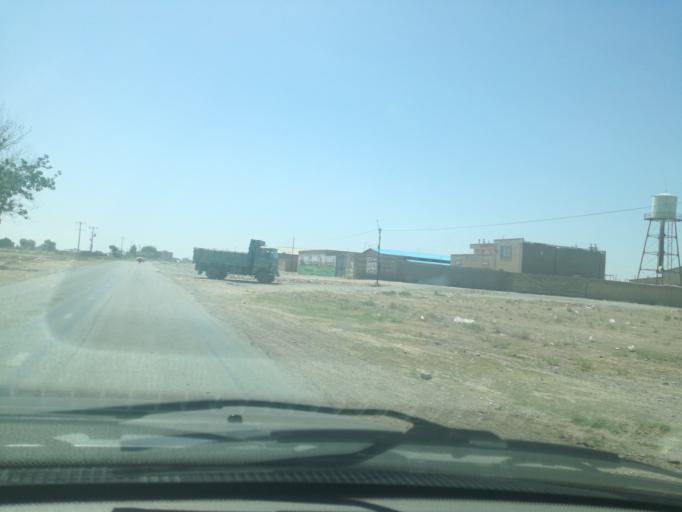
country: IR
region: Razavi Khorasan
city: Sarakhs
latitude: 36.5634
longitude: 61.1456
